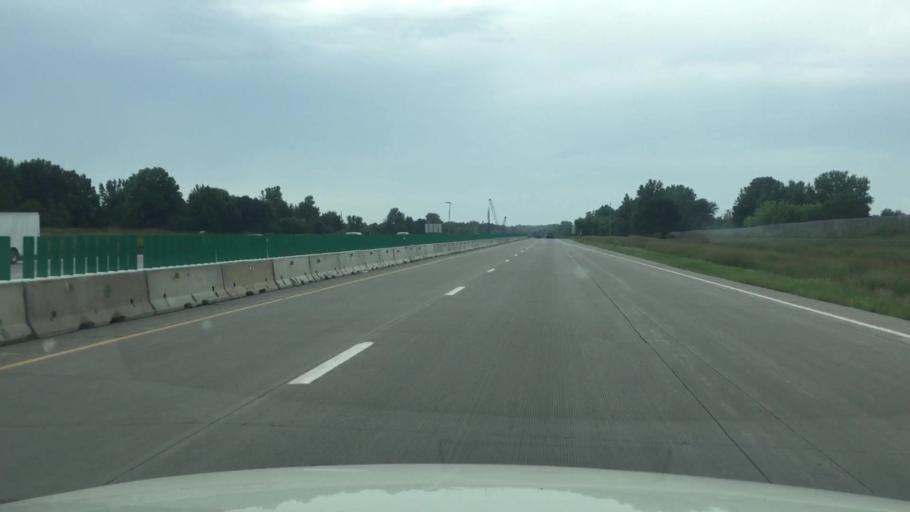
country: US
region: Iowa
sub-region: Polk County
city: Ankeny
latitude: 41.7535
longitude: -93.5732
